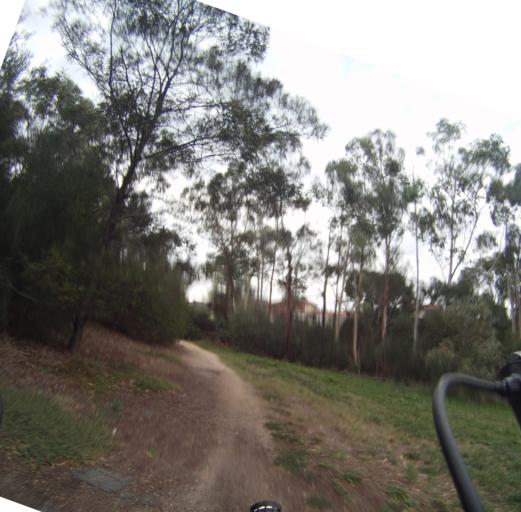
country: AU
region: Victoria
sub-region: Moreland
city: Fawkner
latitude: -37.6947
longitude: 144.9784
